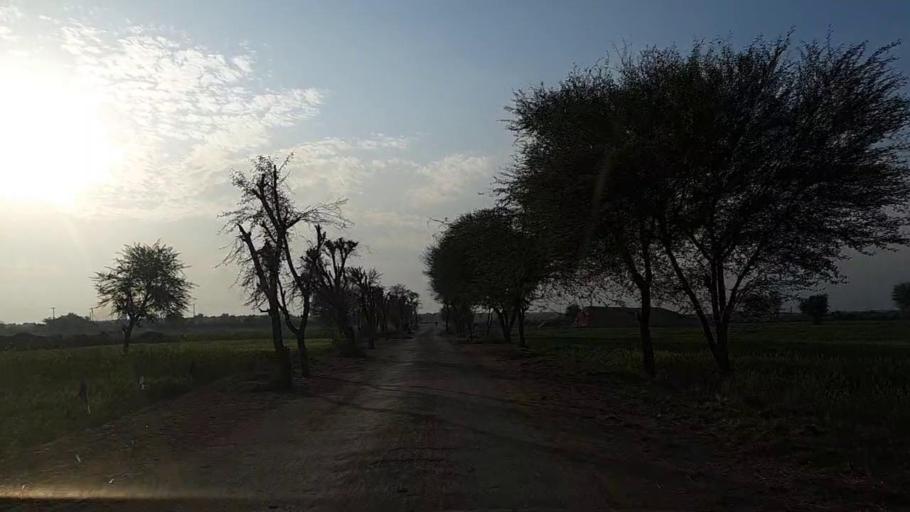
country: PK
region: Sindh
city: Jam Sahib
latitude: 26.3946
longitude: 68.5108
